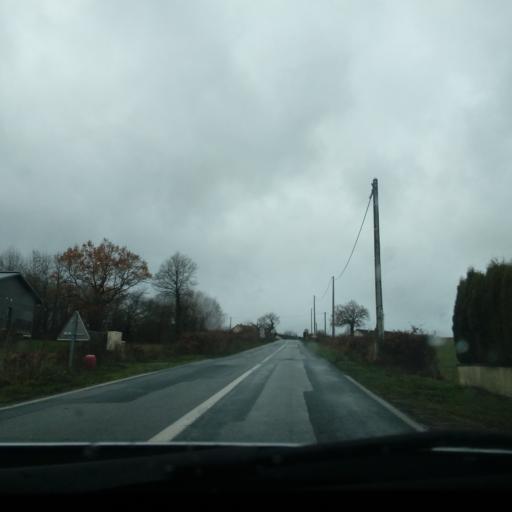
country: FR
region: Limousin
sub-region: Departement de la Creuse
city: Sainte-Feyre
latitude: 46.1760
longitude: 1.9045
